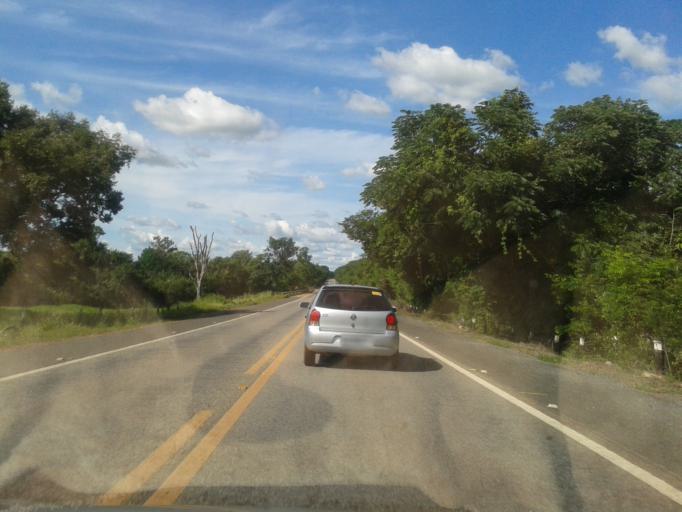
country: BR
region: Goias
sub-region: Mozarlandia
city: Mozarlandia
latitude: -15.0018
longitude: -50.5896
